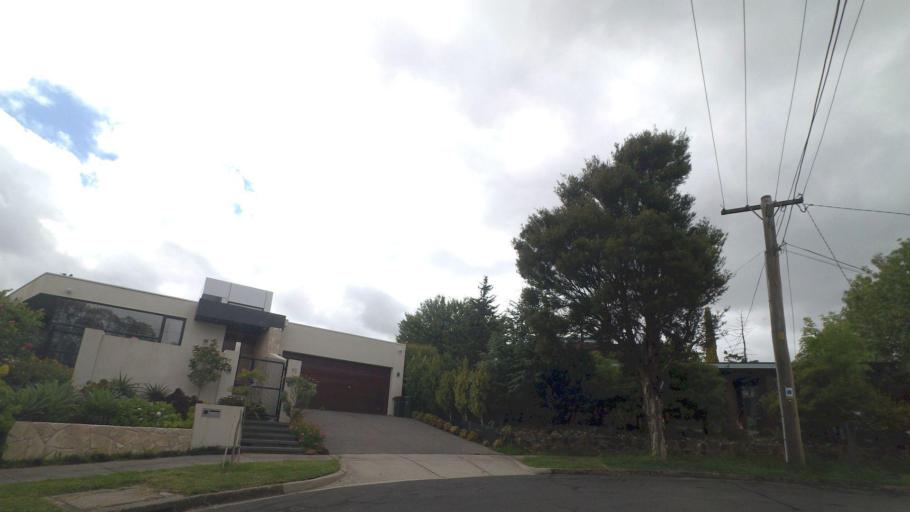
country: AU
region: Victoria
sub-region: Whitehorse
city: Vermont South
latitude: -37.8568
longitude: 145.1765
